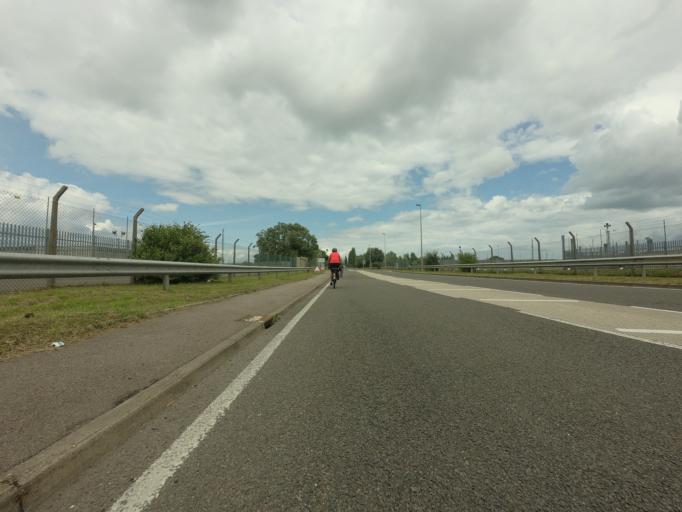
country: GB
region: England
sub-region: Medway
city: Allhallows
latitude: 51.4461
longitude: 0.6927
